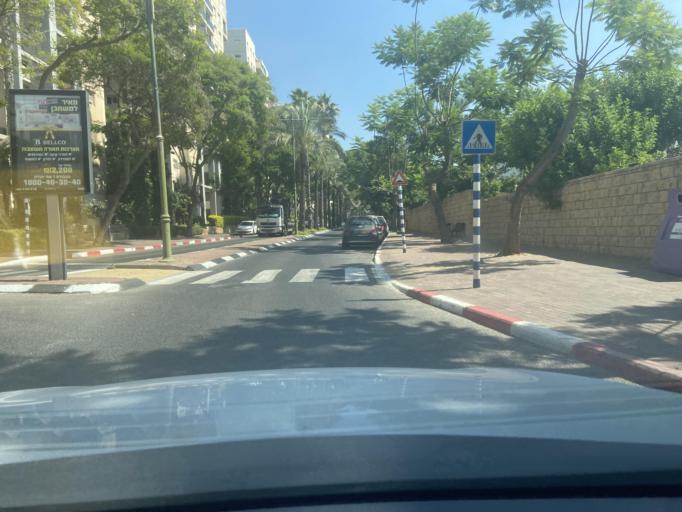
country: IL
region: Central District
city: Yehud
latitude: 32.0325
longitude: 34.8808
